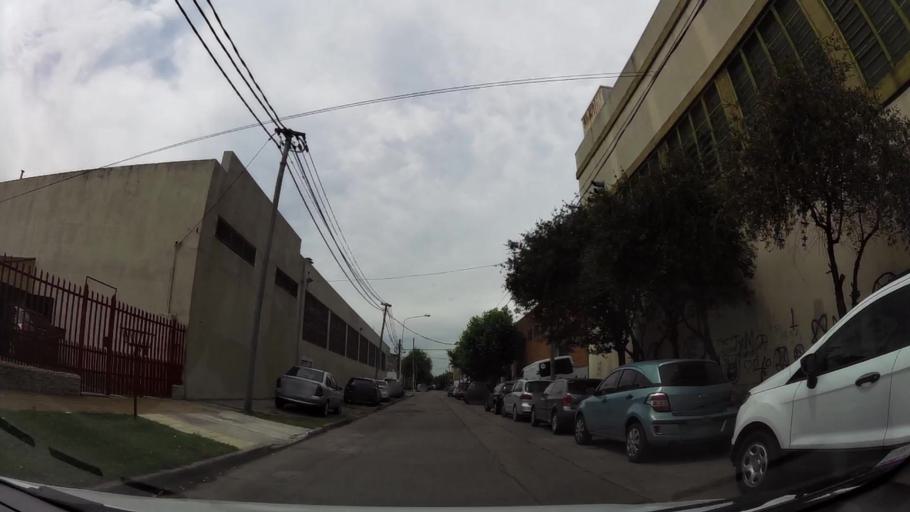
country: AR
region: Buenos Aires
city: San Justo
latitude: -34.6721
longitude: -58.5362
